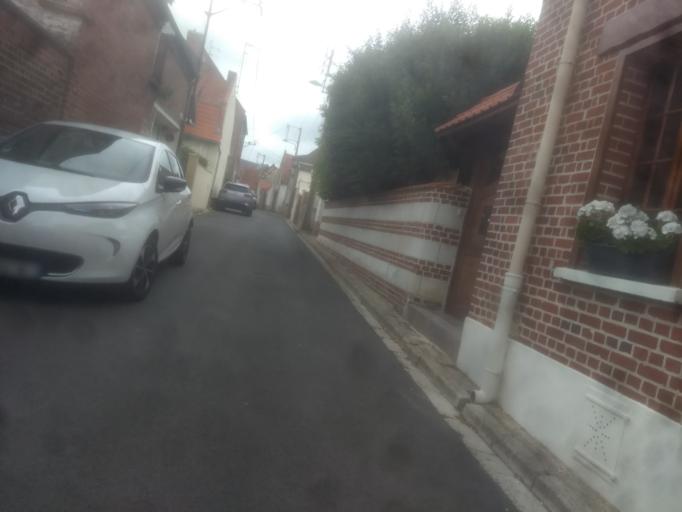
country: FR
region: Nord-Pas-de-Calais
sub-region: Departement du Pas-de-Calais
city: Maroeuil
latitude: 50.3242
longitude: 2.7063
